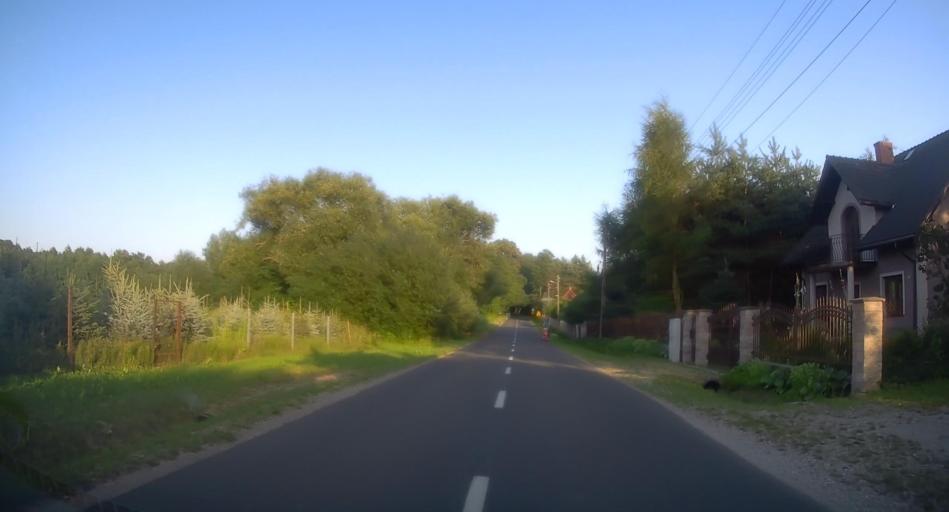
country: PL
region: Lodz Voivodeship
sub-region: Powiat skierniewicki
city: Kowiesy
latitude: 51.8925
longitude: 20.3858
